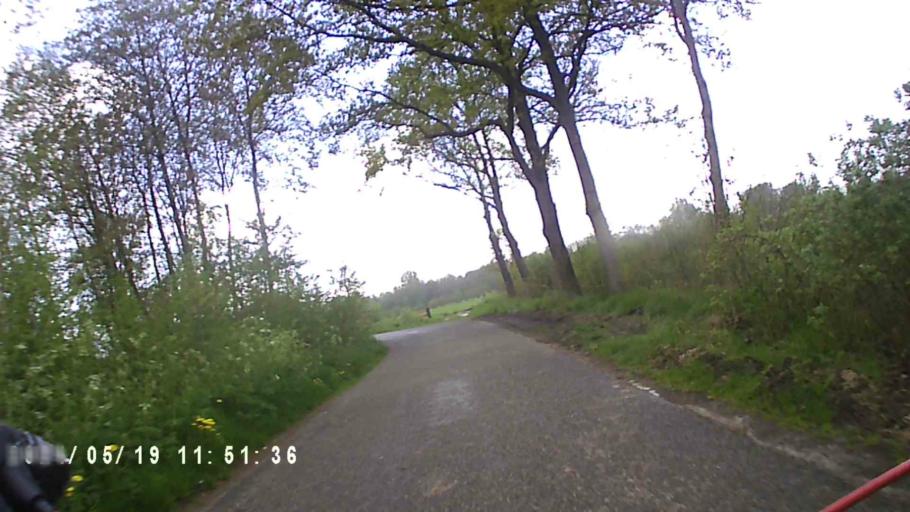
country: NL
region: Friesland
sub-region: Gemeente Kollumerland en Nieuwkruisland
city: Kollum
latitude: 53.2684
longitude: 6.1425
